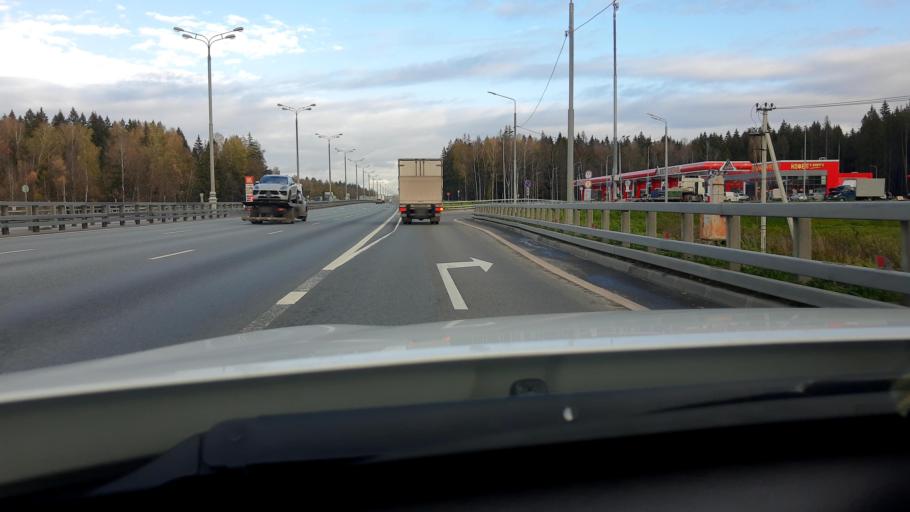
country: RU
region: Moskovskaya
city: Aprelevka
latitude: 55.5503
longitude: 37.1285
